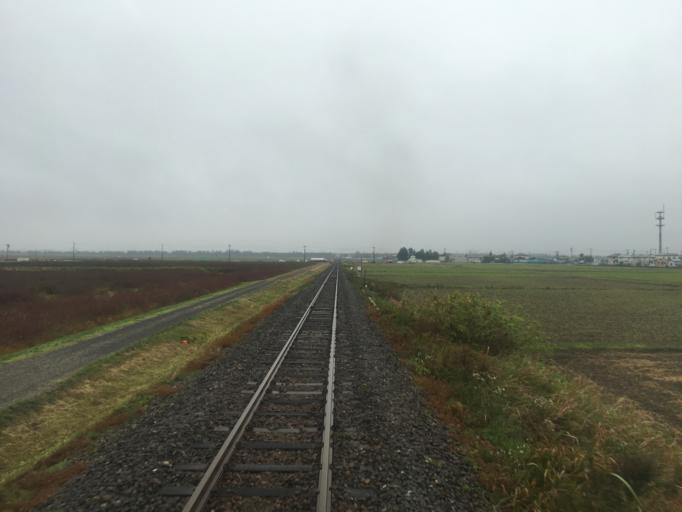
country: JP
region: Miyagi
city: Furukawa
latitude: 38.5741
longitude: 140.9112
